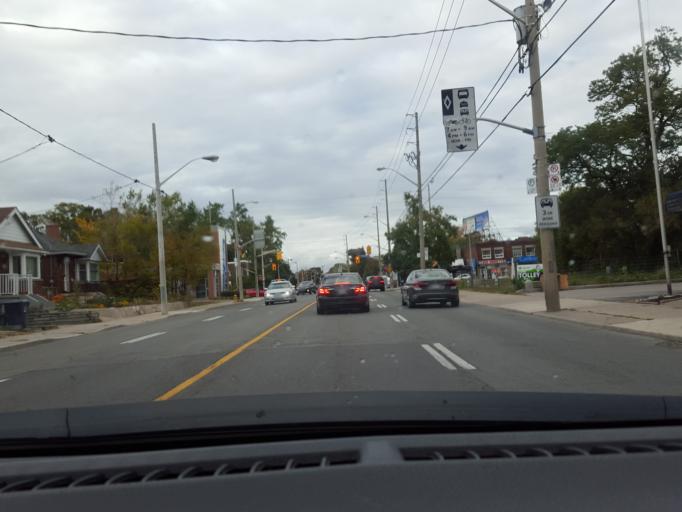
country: CA
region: Ontario
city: Toronto
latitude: 43.6923
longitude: -79.3499
